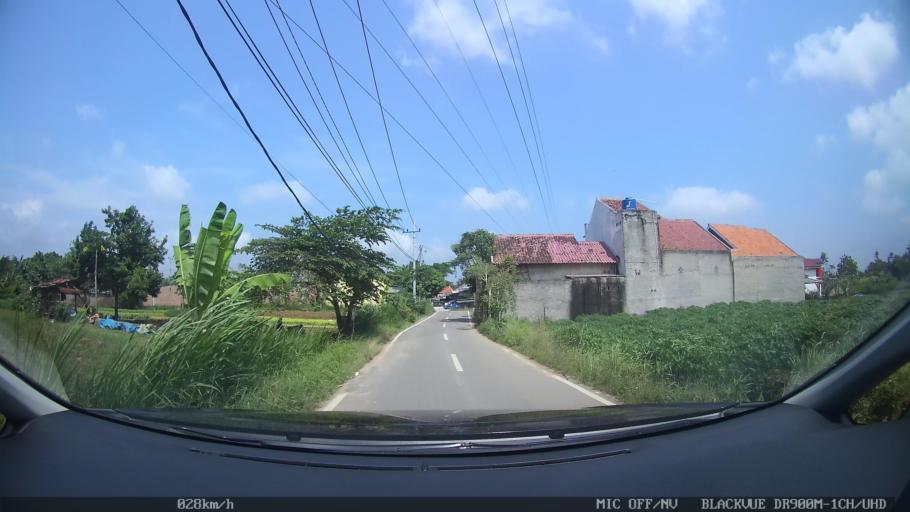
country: ID
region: Lampung
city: Kedaton
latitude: -5.3480
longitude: 105.2775
